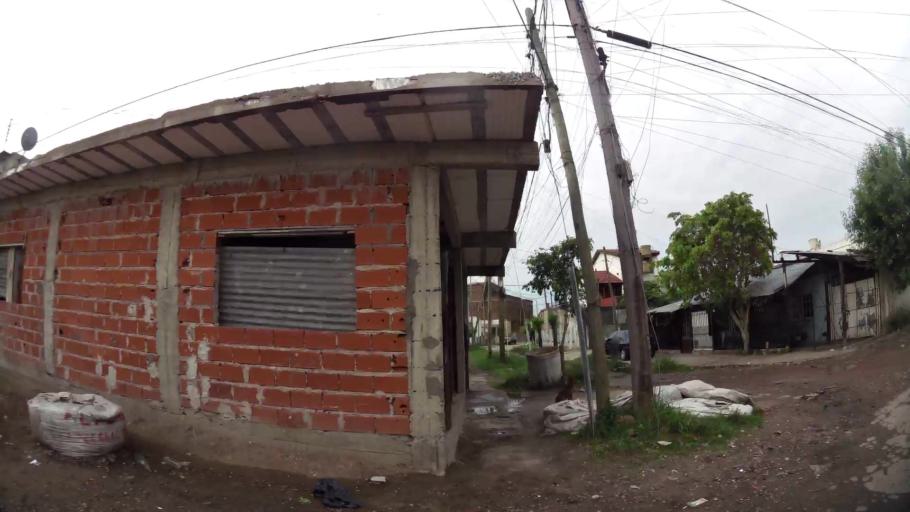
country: AR
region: Buenos Aires
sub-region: Partido de Lanus
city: Lanus
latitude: -34.7249
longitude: -58.3426
